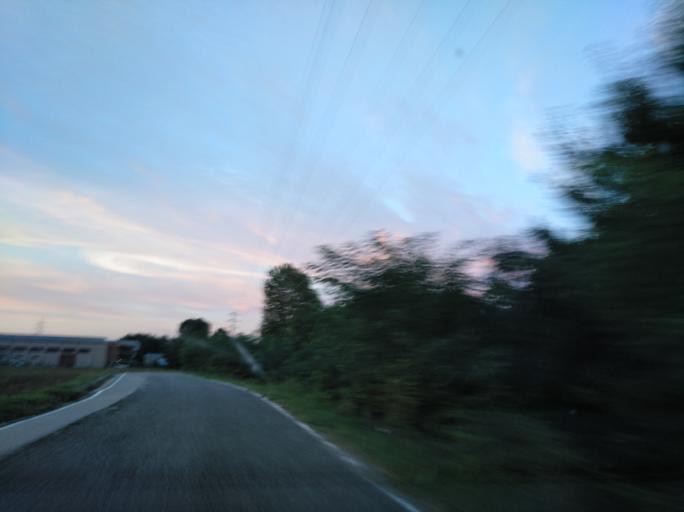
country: ES
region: Catalonia
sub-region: Provincia de Girona
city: Vilablareix
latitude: 41.9560
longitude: 2.7926
